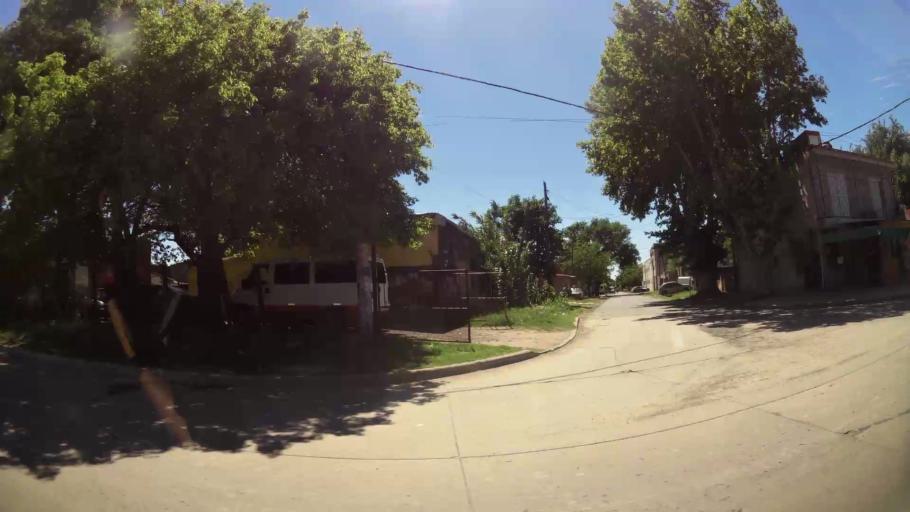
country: AR
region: Santa Fe
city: Perez
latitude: -32.9650
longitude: -60.7188
